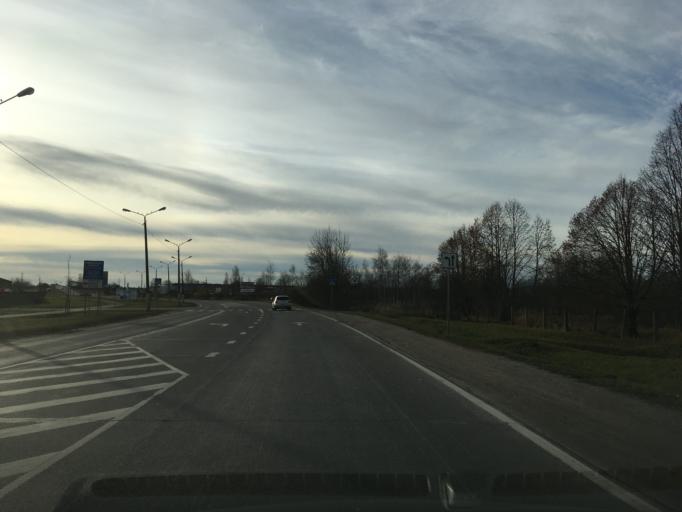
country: EE
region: Ida-Virumaa
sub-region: Narva linn
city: Narva
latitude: 59.3784
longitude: 28.1547
